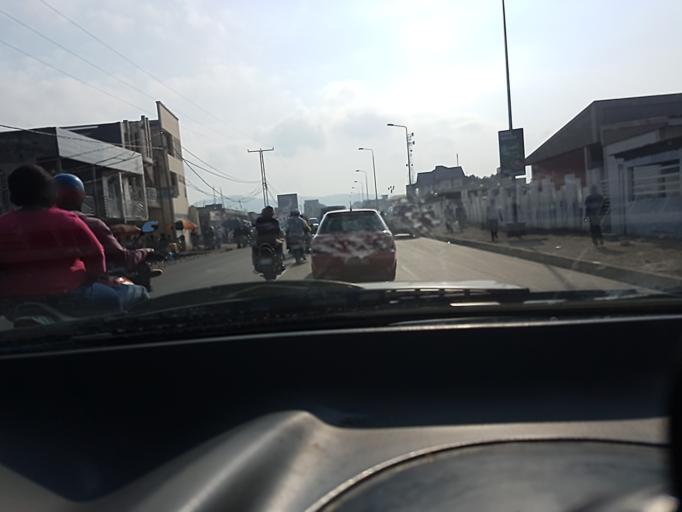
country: CD
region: Nord Kivu
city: Goma
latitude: -1.6784
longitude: 29.2245
